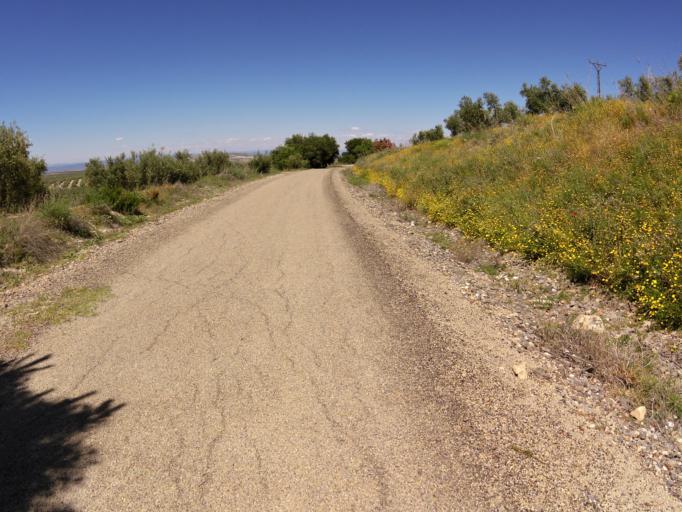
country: ES
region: Andalusia
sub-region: Provincia de Jaen
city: Torre del Campo
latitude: 37.7874
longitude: -3.8889
